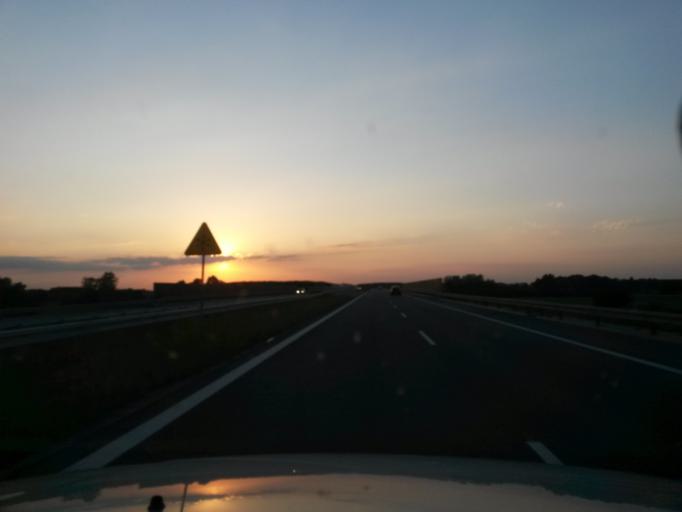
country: PL
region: Lodz Voivodeship
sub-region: Powiat wieruszowski
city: Wieruszow
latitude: 51.3212
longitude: 18.1606
